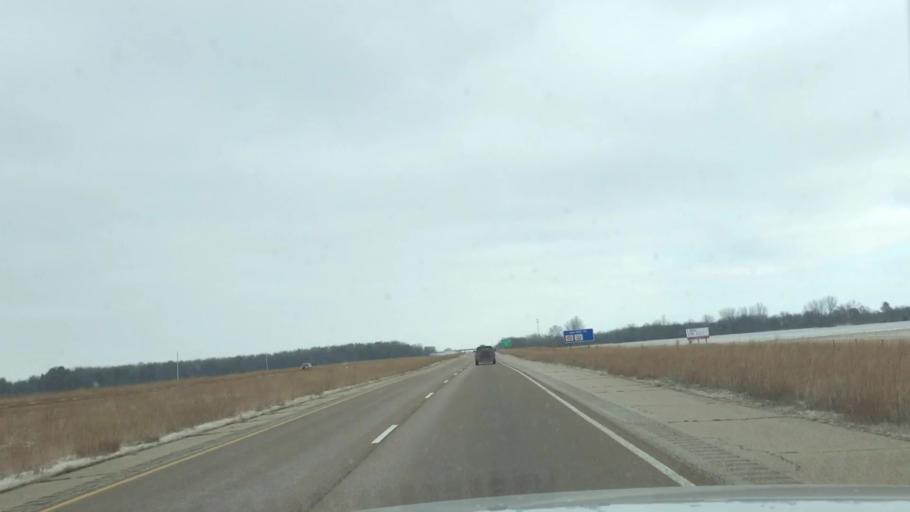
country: US
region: Illinois
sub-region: Montgomery County
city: Raymond
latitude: 39.4273
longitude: -89.6436
